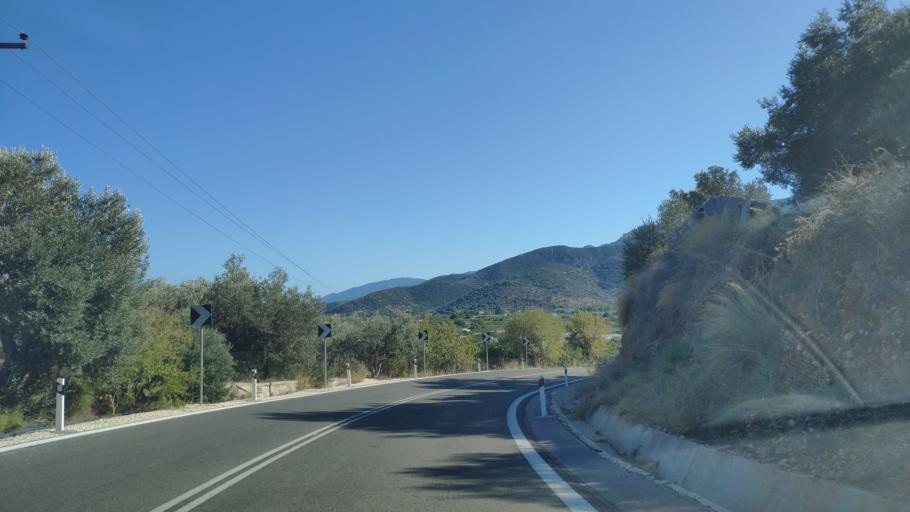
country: GR
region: Peloponnese
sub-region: Nomos Argolidos
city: Didyma
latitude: 37.5482
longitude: 23.2827
